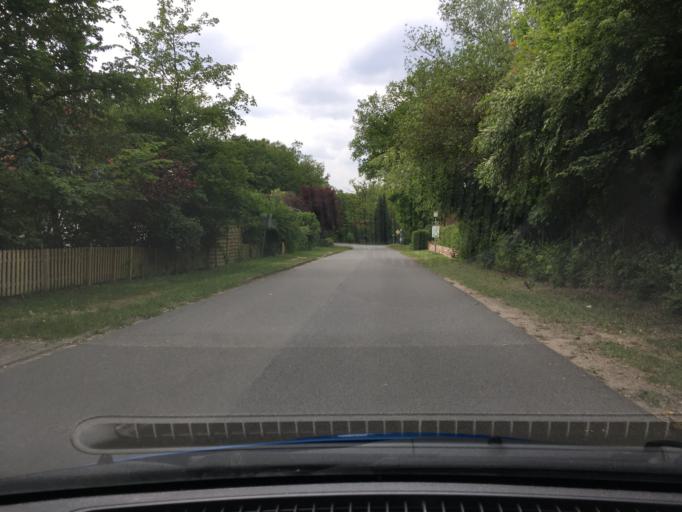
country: DE
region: Lower Saxony
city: Rehlingen
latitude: 53.1042
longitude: 10.2238
